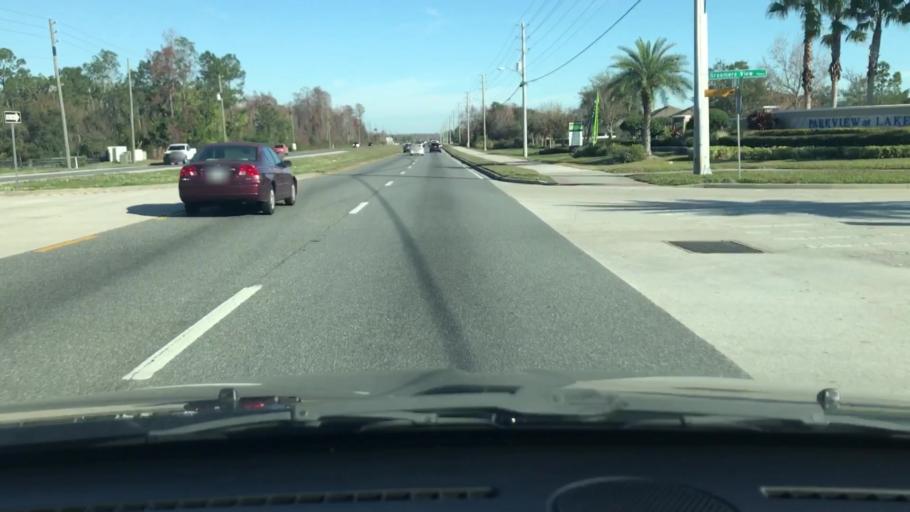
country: US
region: Florida
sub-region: Osceola County
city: Campbell
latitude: 28.2060
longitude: -81.4399
